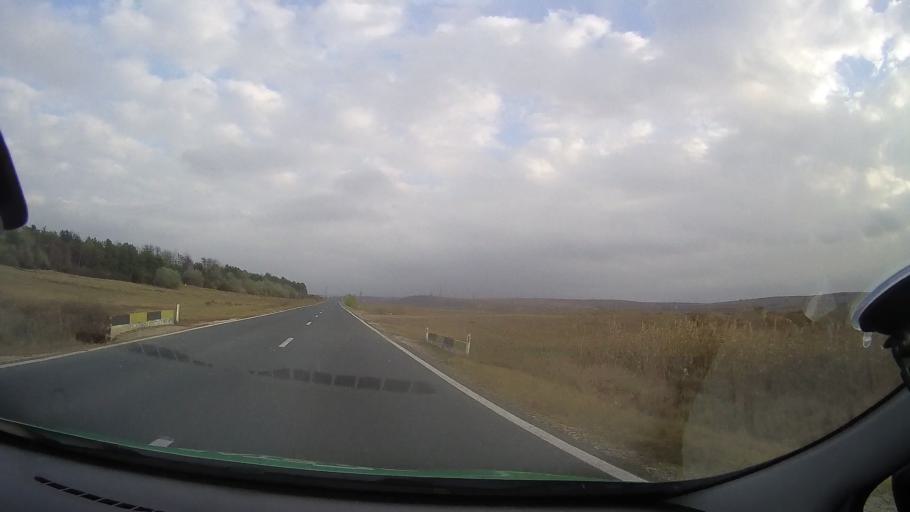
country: RO
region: Constanta
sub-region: Comuna Mircea Voda
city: Mircea Voda
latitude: 44.2696
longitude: 28.1765
